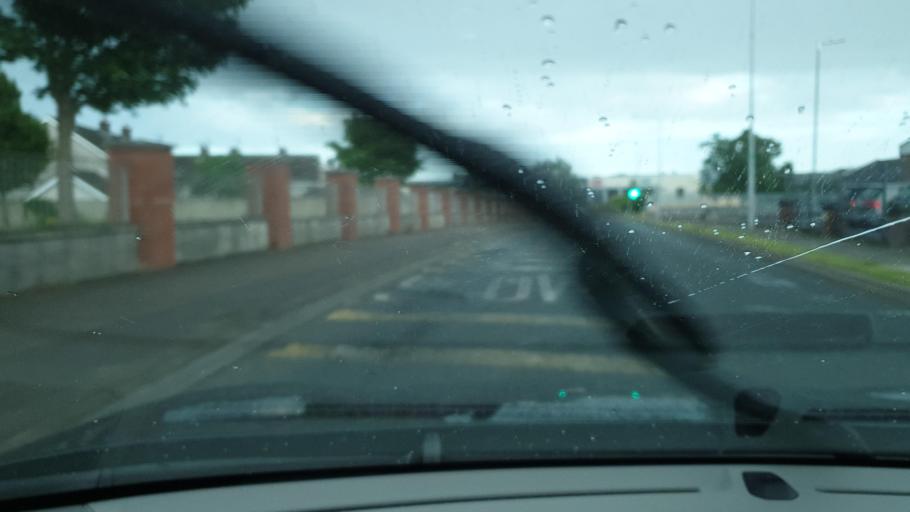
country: IE
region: Leinster
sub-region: An Mhi
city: Navan
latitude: 53.6462
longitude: -6.6980
